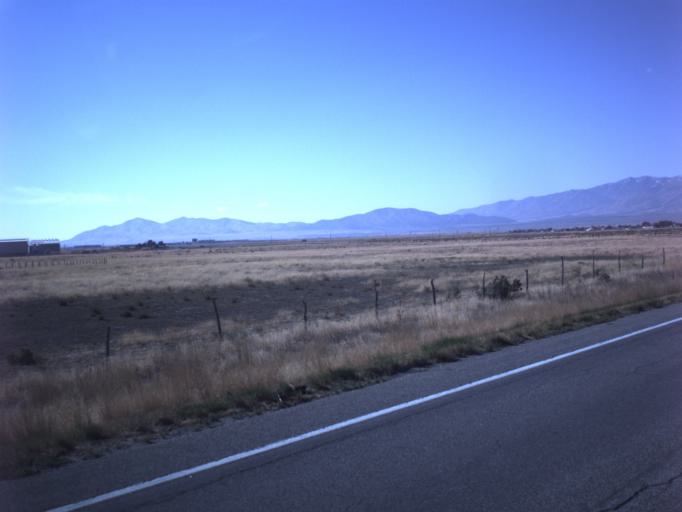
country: US
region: Utah
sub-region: Tooele County
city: Erda
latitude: 40.6109
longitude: -112.3780
